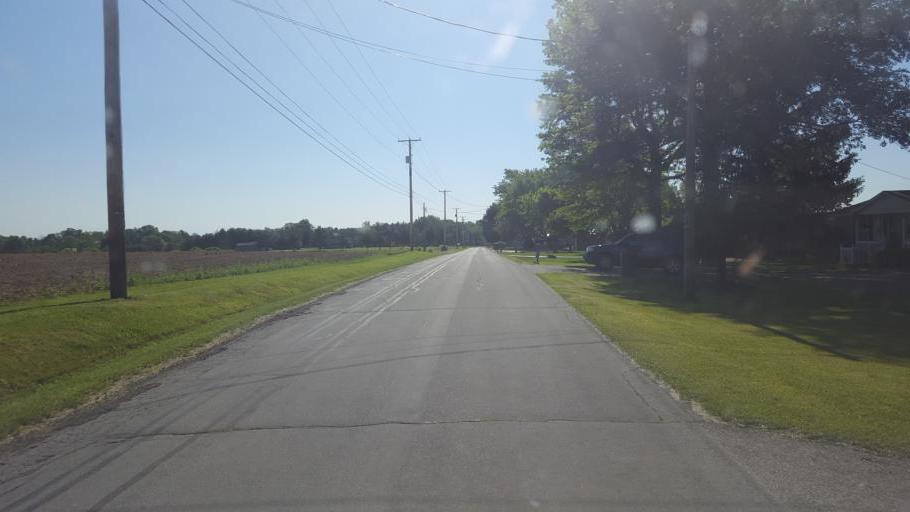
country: US
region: Ohio
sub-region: Crawford County
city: Galion
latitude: 40.7704
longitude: -82.7992
